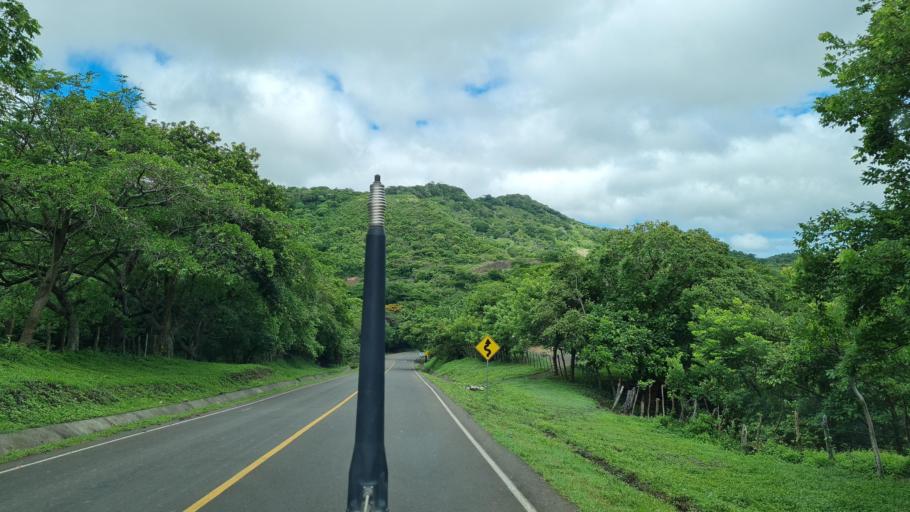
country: NI
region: Matagalpa
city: Terrabona
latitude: 12.5908
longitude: -85.9386
